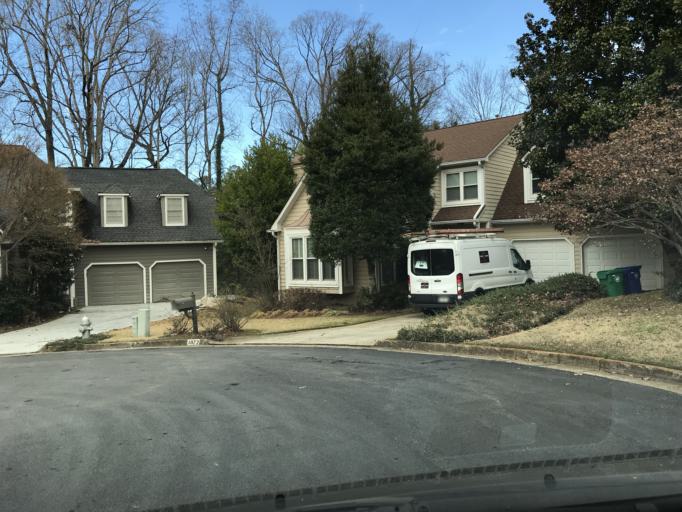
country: US
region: Georgia
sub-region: DeKalb County
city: North Atlanta
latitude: 33.8783
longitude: -84.3450
